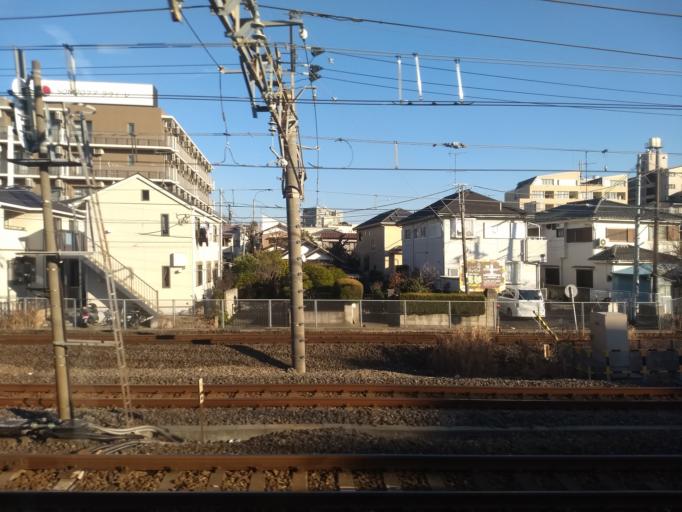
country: JP
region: Chiba
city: Matsudo
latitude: 35.8128
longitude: 139.9176
